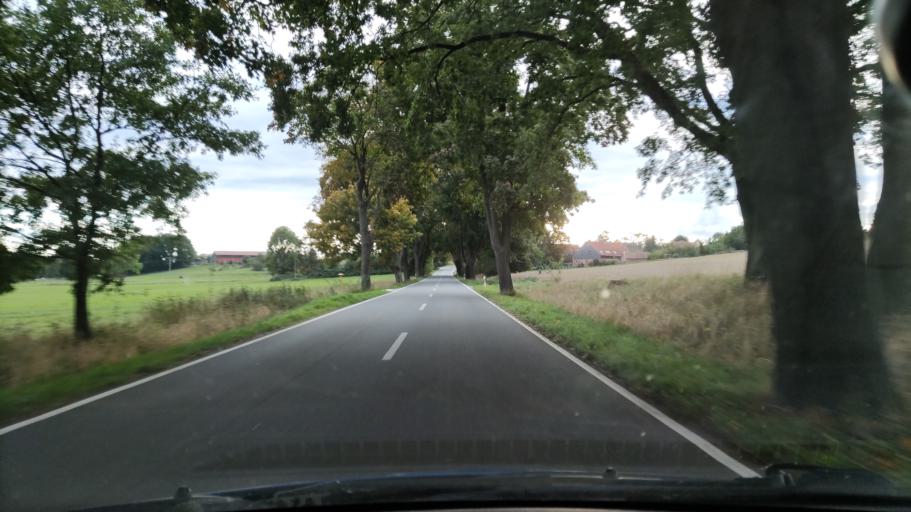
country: DE
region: Schleswig-Holstein
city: Langenlehsten
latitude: 53.4295
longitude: 10.8489
